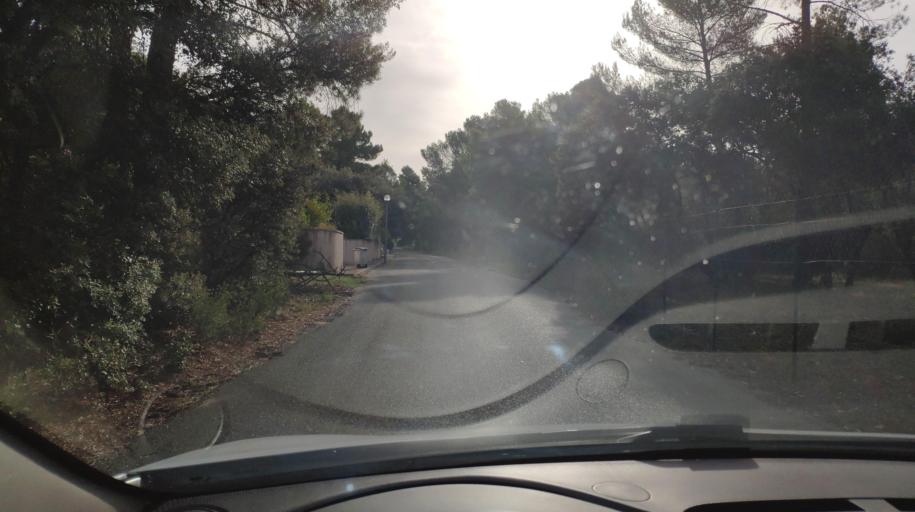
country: FR
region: Provence-Alpes-Cote d'Azur
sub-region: Departement du Vaucluse
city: Bedoin
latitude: 44.1172
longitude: 5.1860
